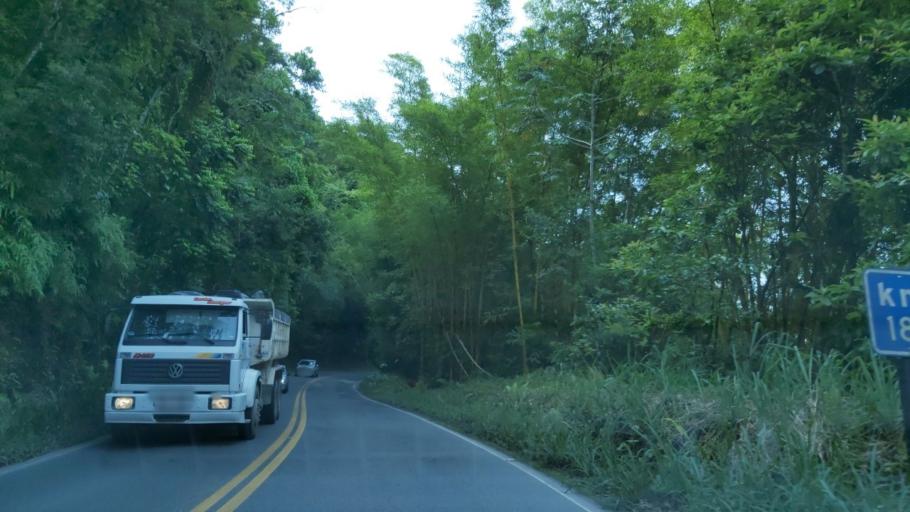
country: BR
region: Sao Paulo
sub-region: Juquia
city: Juquia
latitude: -24.1080
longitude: -47.6281
